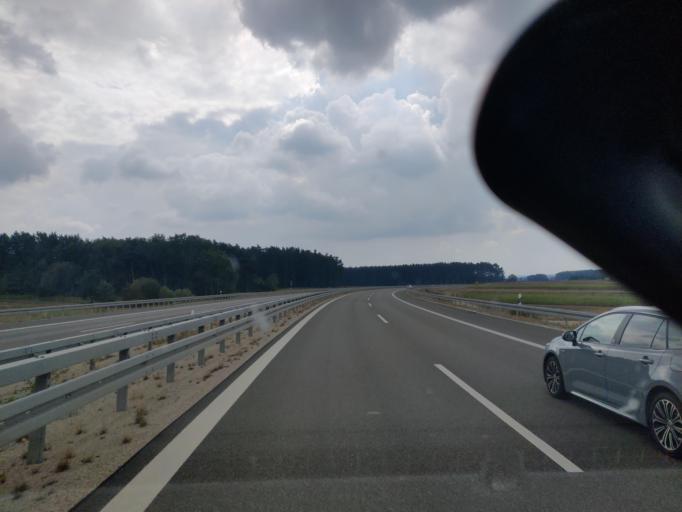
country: DE
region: Bavaria
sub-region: Regierungsbezirk Mittelfranken
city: Rottenbach
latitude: 49.1798
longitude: 11.0775
